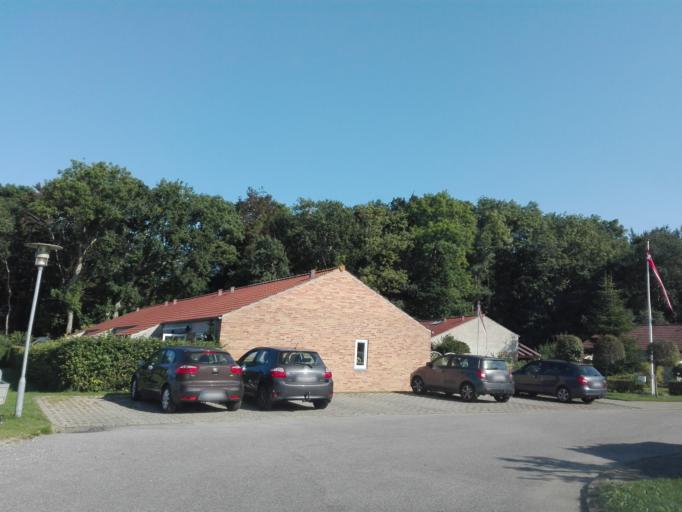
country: DK
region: Central Jutland
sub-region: Odder Kommune
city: Odder
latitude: 55.9234
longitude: 10.2501
